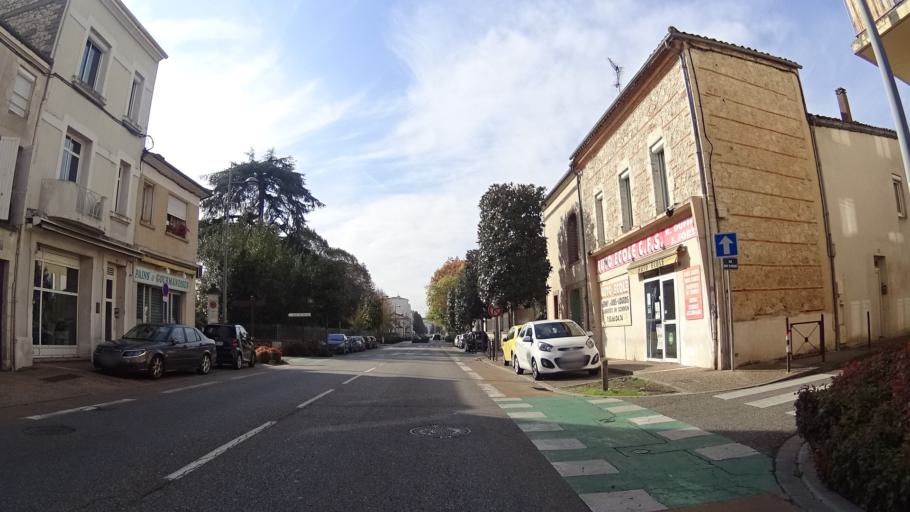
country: FR
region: Aquitaine
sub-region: Departement du Lot-et-Garonne
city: Agen
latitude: 44.2011
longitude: 0.6228
